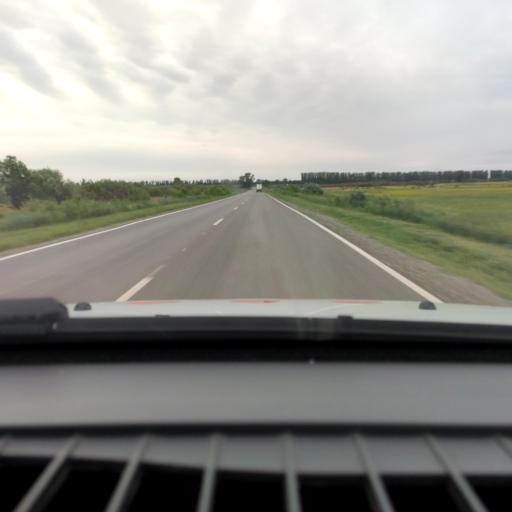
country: RU
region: Voronezj
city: Podkletnoye
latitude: 51.5888
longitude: 39.5142
